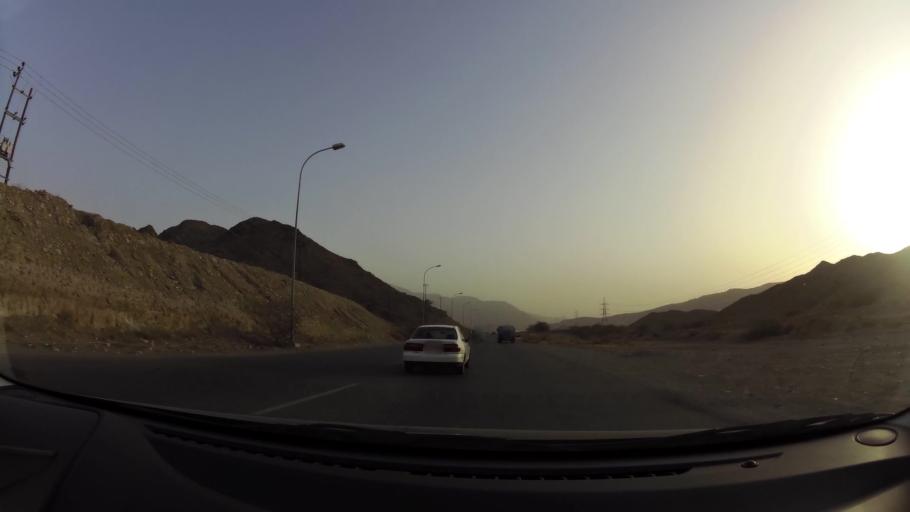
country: OM
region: Muhafazat Masqat
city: Bawshar
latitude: 23.4973
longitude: 58.3255
